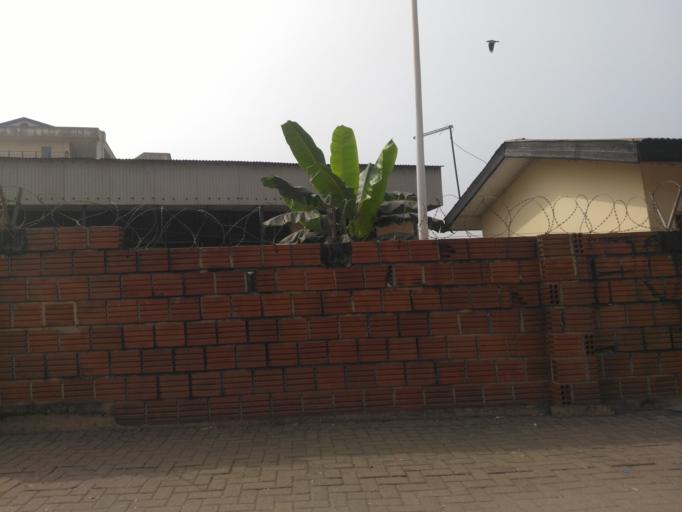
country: GH
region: Ashanti
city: Kumasi
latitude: 6.6917
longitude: -1.6090
